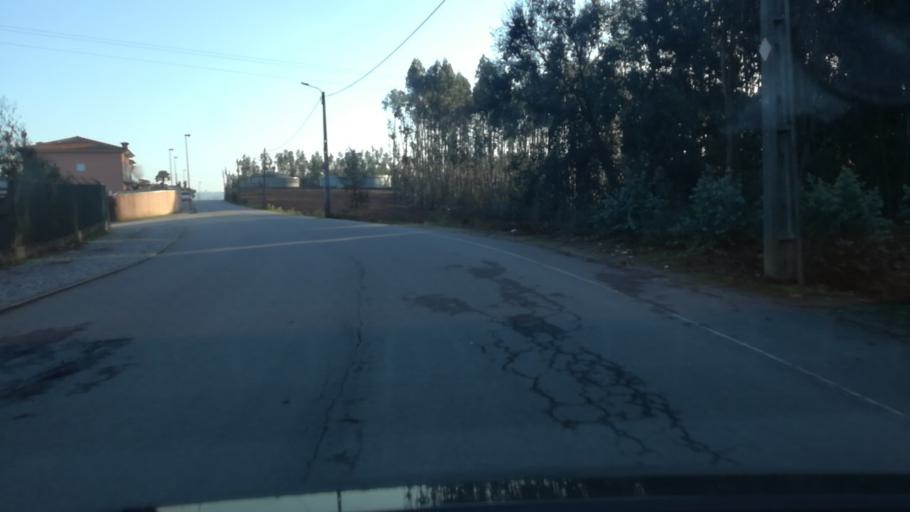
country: PT
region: Braga
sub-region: Vila Nova de Famalicao
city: Ferreiros
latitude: 41.3629
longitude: -8.5327
